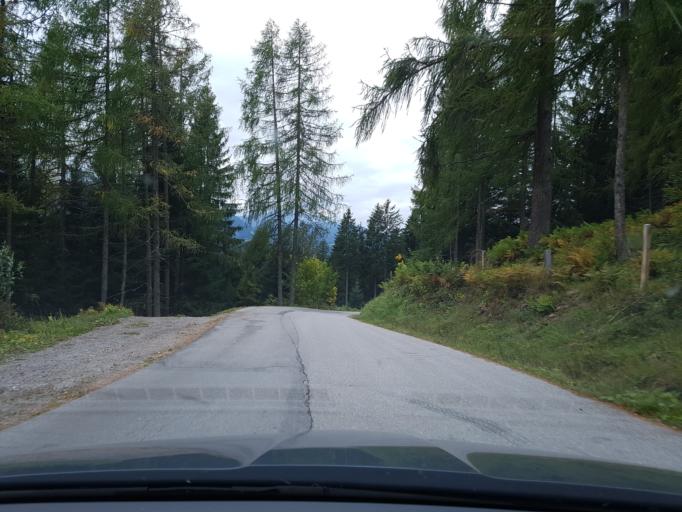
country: AT
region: Salzburg
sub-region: Politischer Bezirk Sankt Johann im Pongau
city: Filzmoos
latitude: 47.3965
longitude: 13.4931
